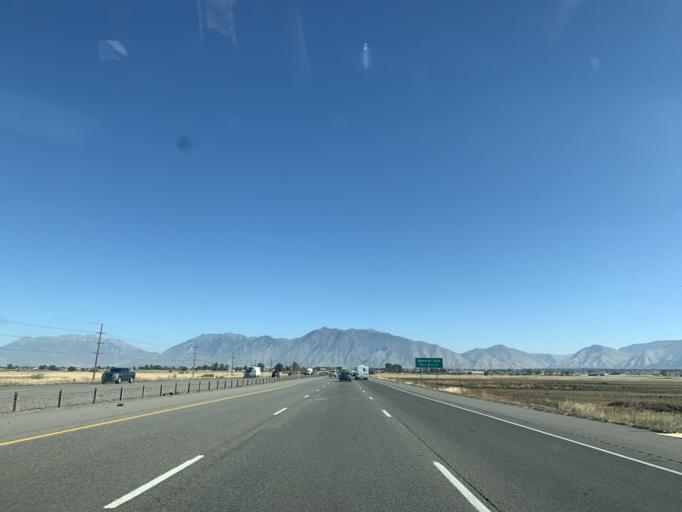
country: US
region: Utah
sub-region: Utah County
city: Payson
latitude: 40.0663
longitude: -111.7220
